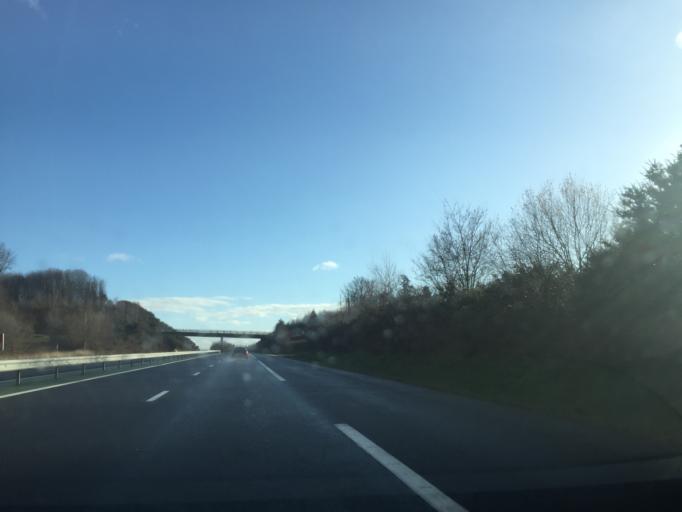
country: FR
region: Limousin
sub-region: Departement de la Correze
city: Saint-Clement
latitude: 45.3073
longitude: 1.6768
